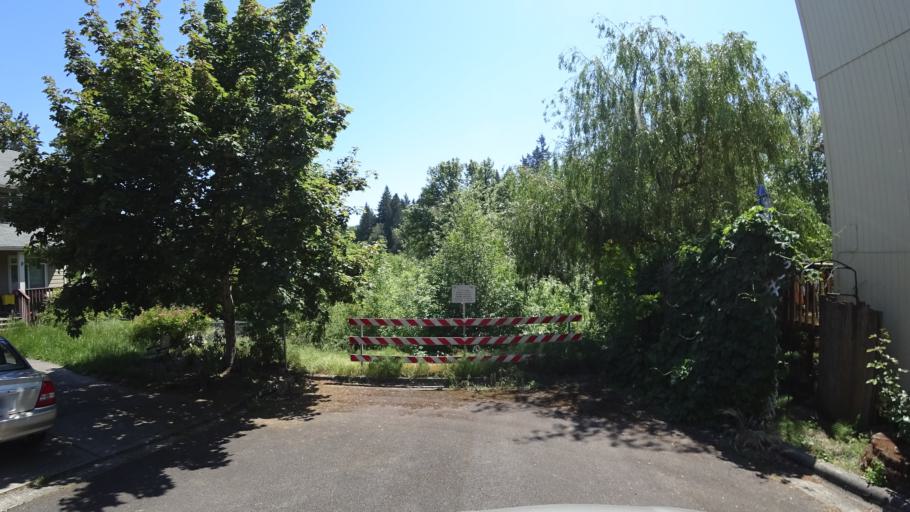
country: US
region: Oregon
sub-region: Washington County
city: Rockcreek
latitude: 45.5219
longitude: -122.9040
